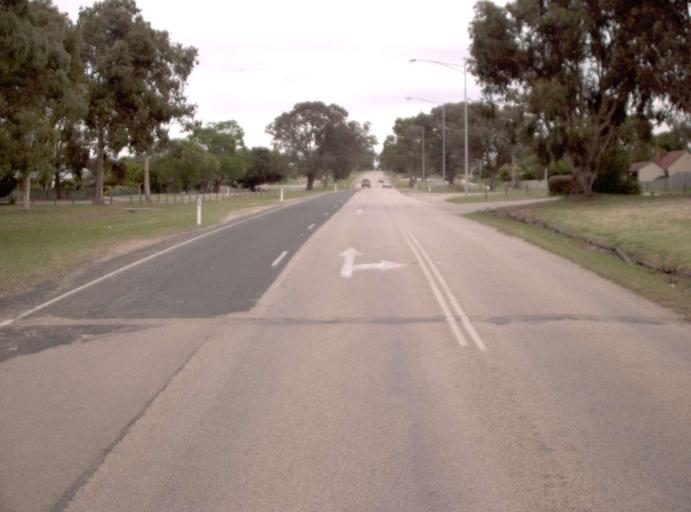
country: AU
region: Victoria
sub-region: East Gippsland
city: Bairnsdale
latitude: -37.8071
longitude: 147.6183
